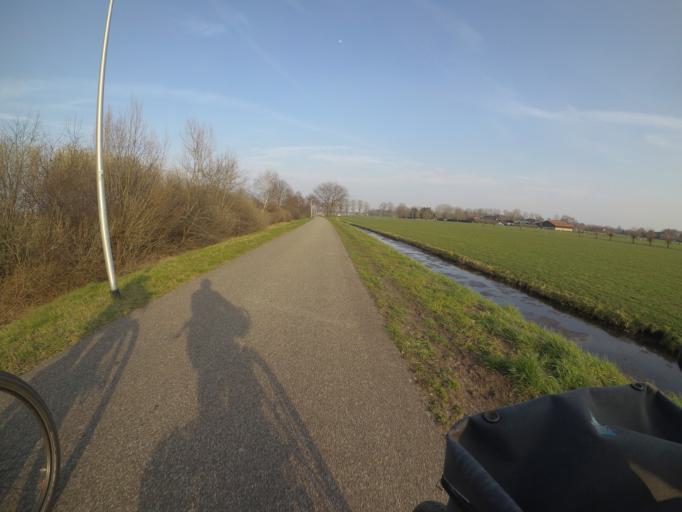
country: NL
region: North Brabant
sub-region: Gemeente Waalwijk
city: Waspik
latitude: 51.6798
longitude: 4.9600
